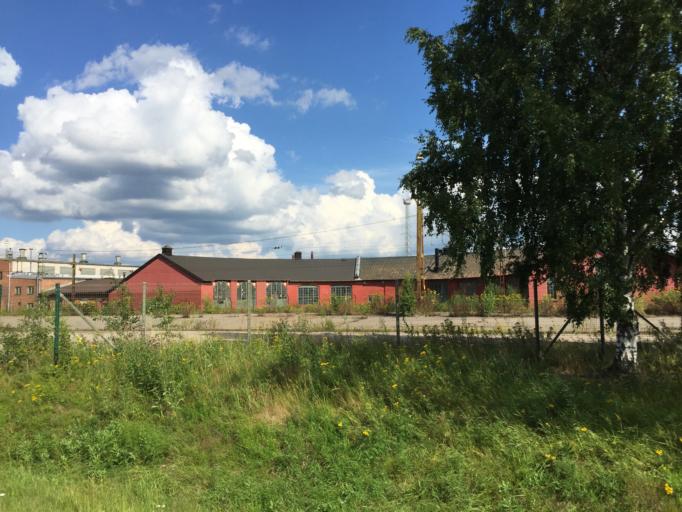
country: SE
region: Gaevleborg
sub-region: Bollnas Kommun
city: Bollnas
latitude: 61.3530
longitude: 16.3920
